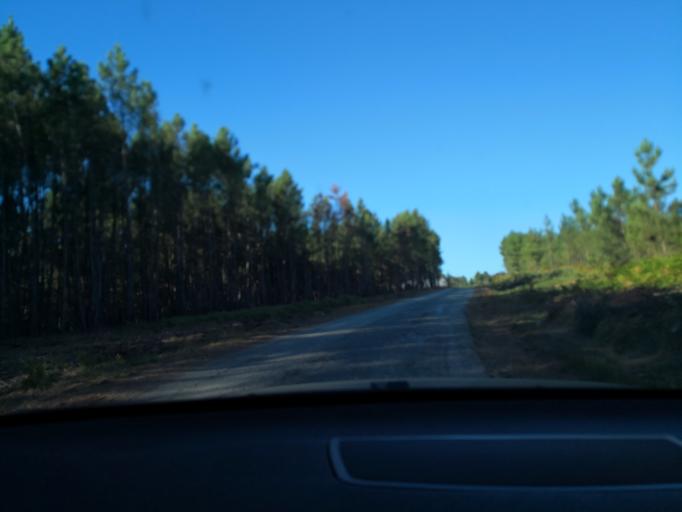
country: PT
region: Vila Real
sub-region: Sabrosa
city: Vilela
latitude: 41.2523
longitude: -7.6259
